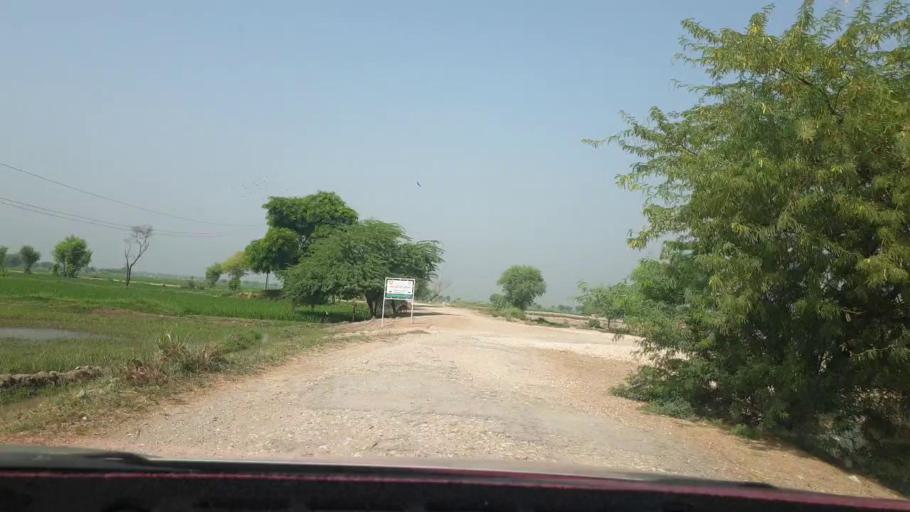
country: PK
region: Sindh
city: Nasirabad
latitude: 27.4320
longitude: 67.8881
